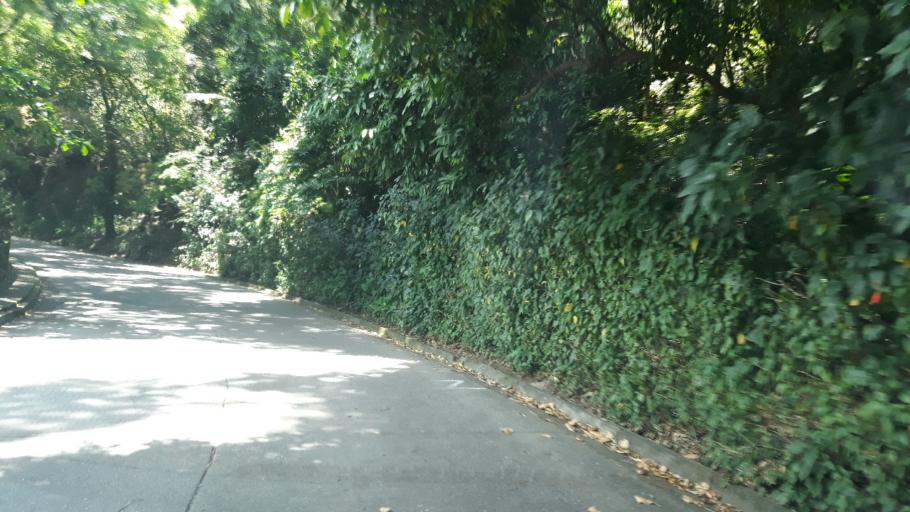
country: BR
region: Rio de Janeiro
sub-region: Rio De Janeiro
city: Rio de Janeiro
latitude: -22.9468
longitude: -43.2062
